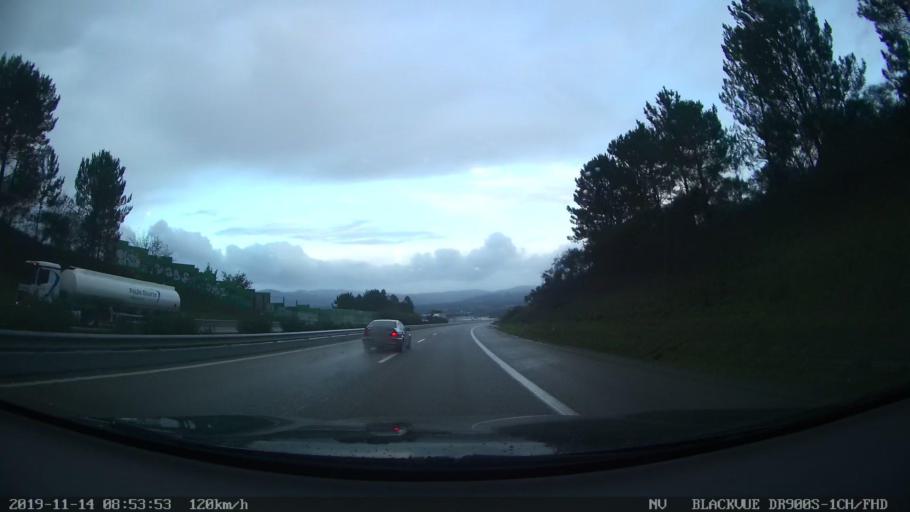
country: PT
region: Viana do Castelo
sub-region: Vila Nova de Cerveira
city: Vila Nova de Cerveira
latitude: 41.9499
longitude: -8.6708
